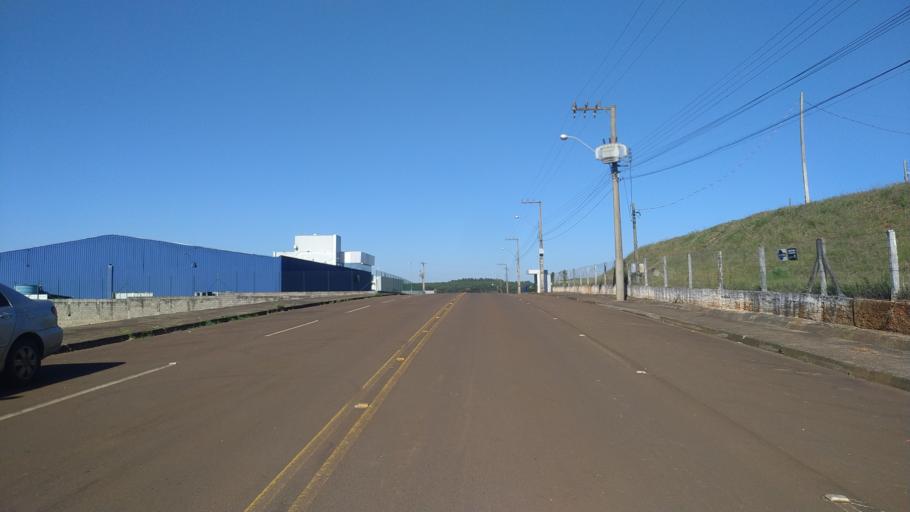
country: BR
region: Santa Catarina
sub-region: Chapeco
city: Chapeco
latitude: -27.1572
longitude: -52.6026
